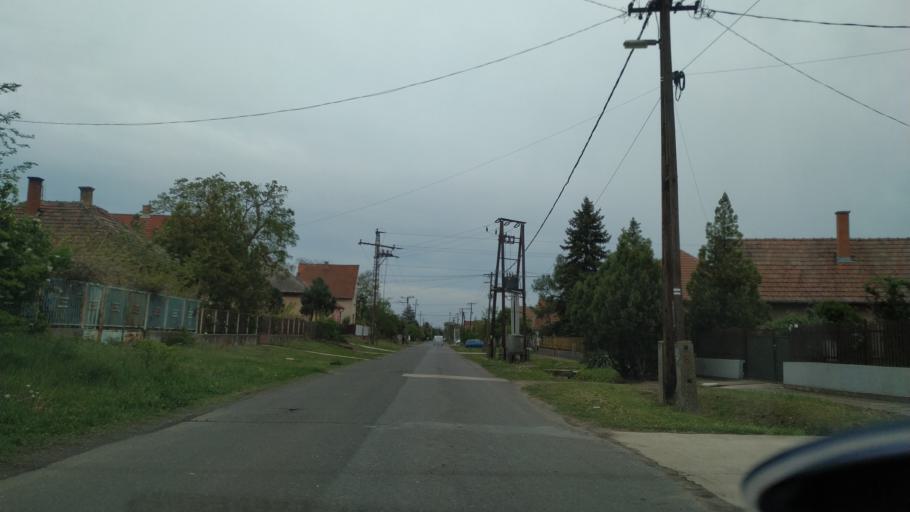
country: HU
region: Pest
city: Nagykata
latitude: 47.4190
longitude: 19.7268
